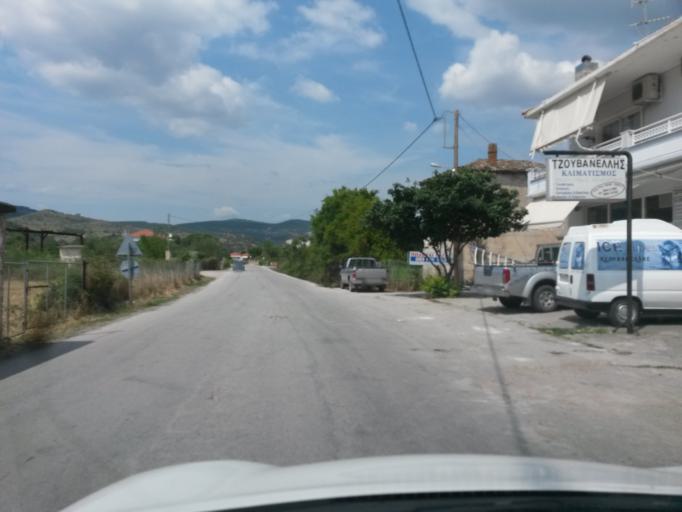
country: GR
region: North Aegean
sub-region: Nomos Lesvou
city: Kalloni
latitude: 39.2361
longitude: 26.2088
